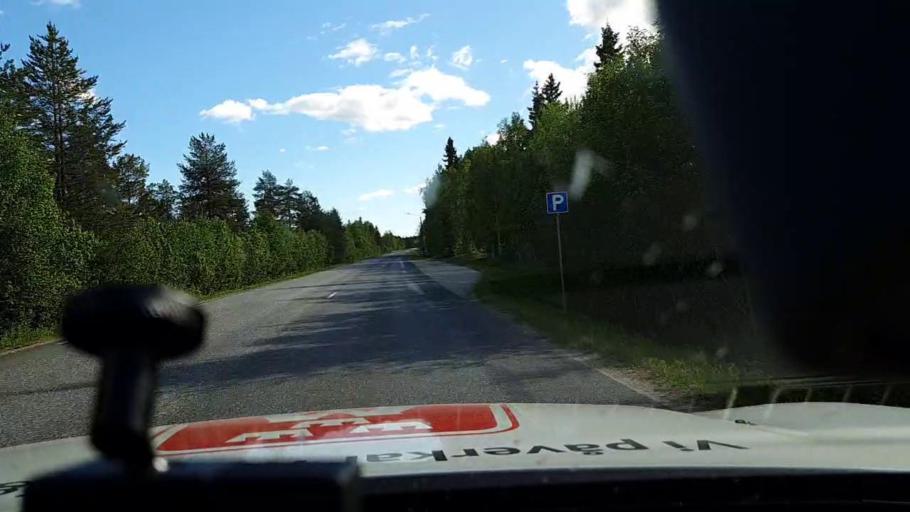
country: FI
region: Lapland
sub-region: Torniolaakso
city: Ylitornio
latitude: 66.3417
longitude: 23.6471
